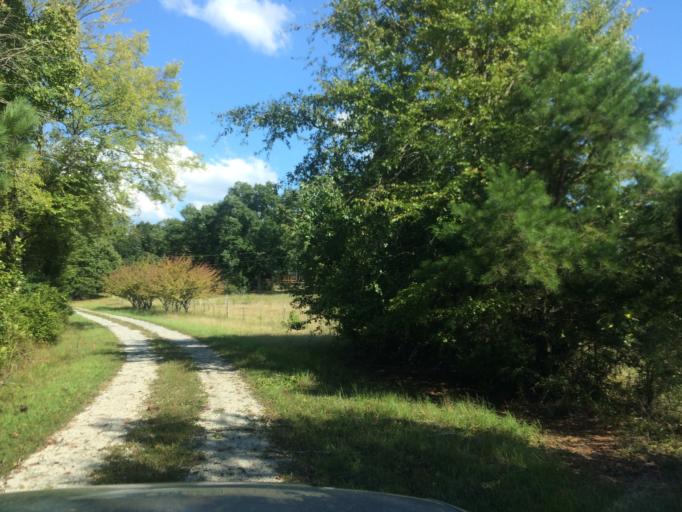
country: US
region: South Carolina
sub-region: Greenwood County
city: Ware Shoals
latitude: 34.4625
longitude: -82.1678
